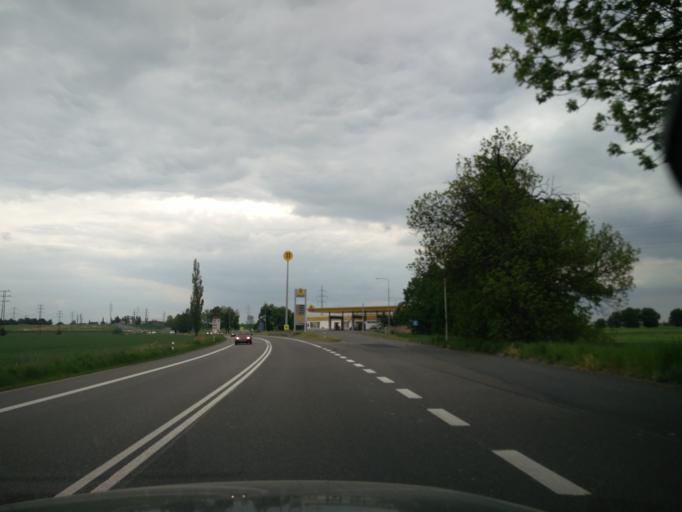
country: CZ
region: Jihocesky
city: Mirovice
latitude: 49.5247
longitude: 14.0731
